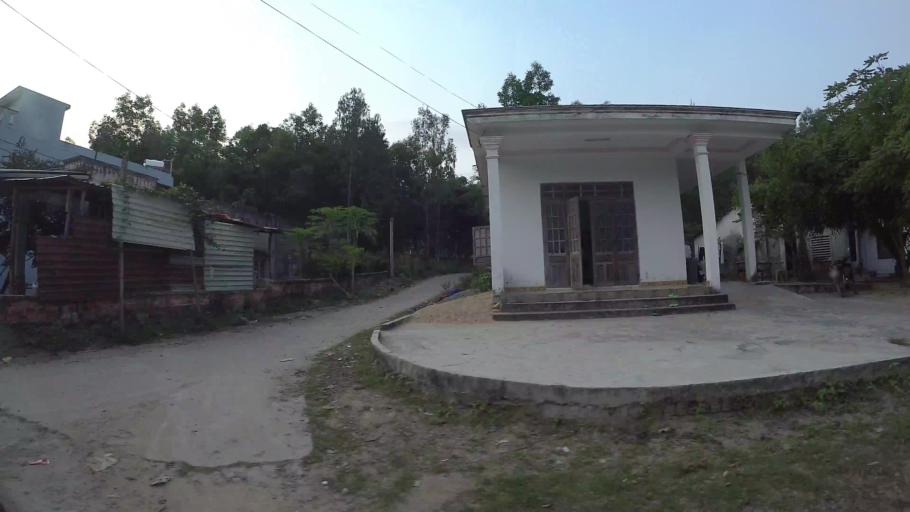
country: VN
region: Da Nang
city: Lien Chieu
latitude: 16.0587
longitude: 108.1197
